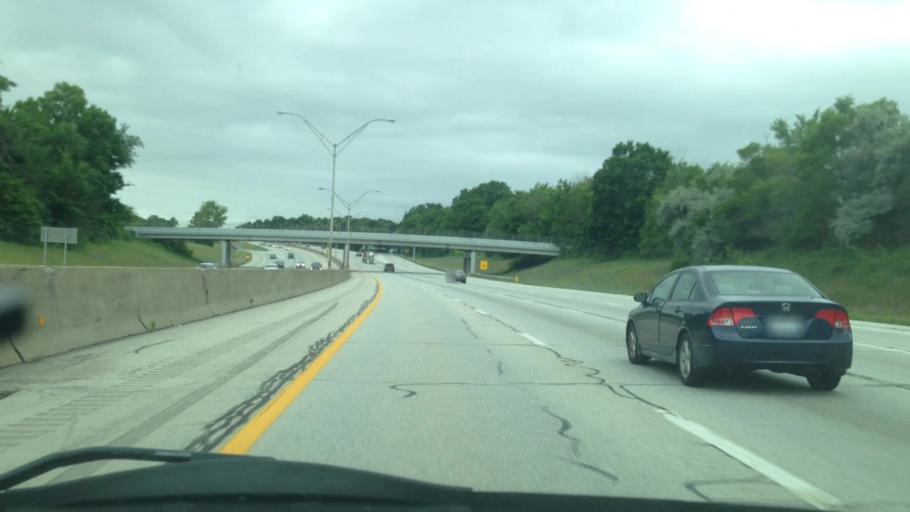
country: US
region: Ohio
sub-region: Cuyahoga County
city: Fairview Park
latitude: 41.4244
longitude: -81.8697
